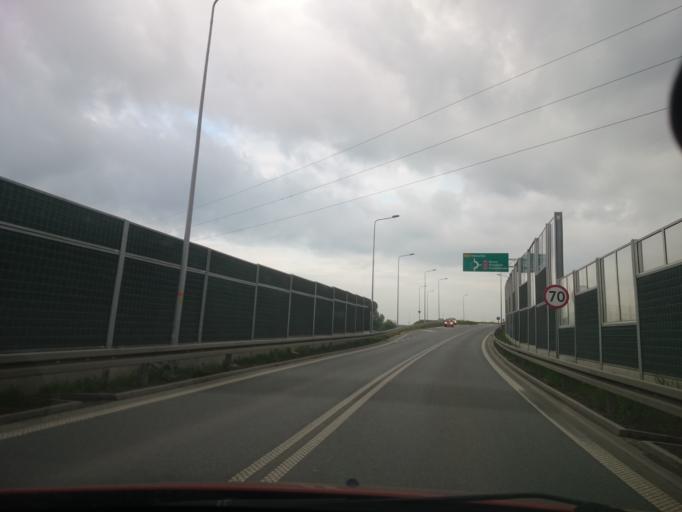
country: PL
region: Opole Voivodeship
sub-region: Powiat opolski
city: Czarnowasy
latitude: 50.6998
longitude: 17.9055
